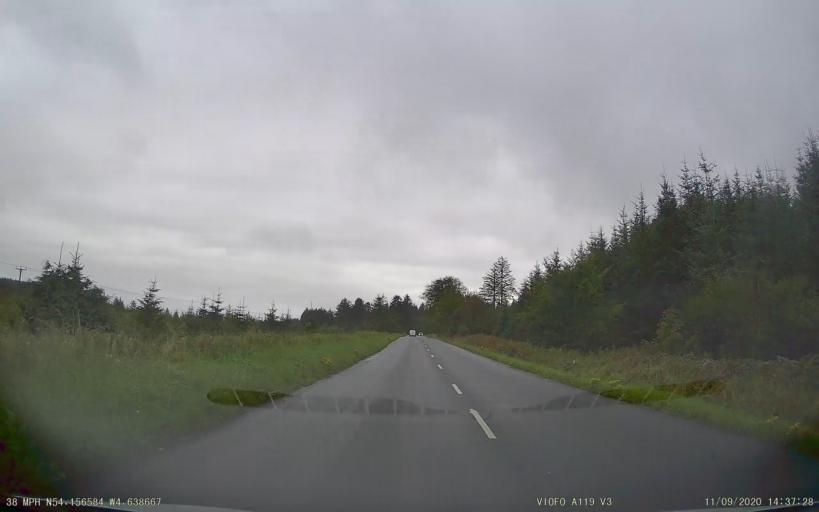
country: IM
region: Castletown
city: Castletown
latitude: 54.1566
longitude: -4.6386
